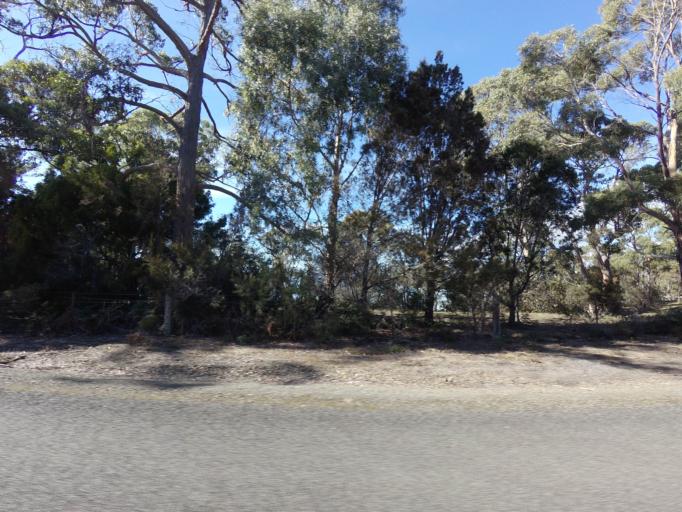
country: AU
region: Tasmania
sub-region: Clarence
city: Sandford
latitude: -43.0031
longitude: 147.7075
